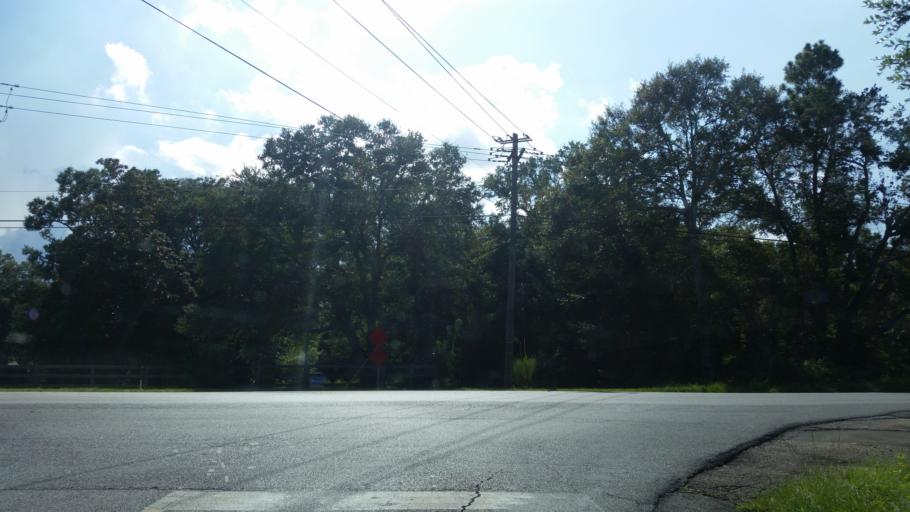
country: US
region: Florida
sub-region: Santa Rosa County
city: Pace
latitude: 30.6187
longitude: -87.1608
